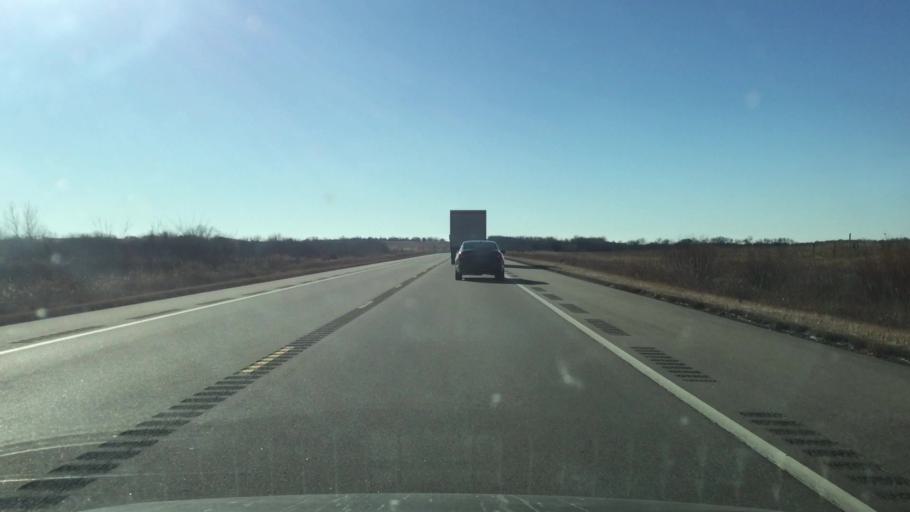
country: US
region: Kansas
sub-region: Allen County
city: Iola
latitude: 38.0290
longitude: -95.3806
